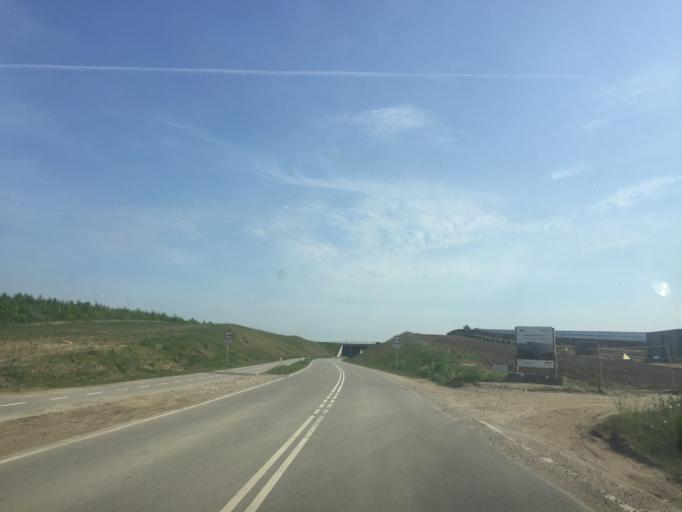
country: DK
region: Capital Region
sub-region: Egedal Kommune
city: Smorumnedre
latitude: 55.7212
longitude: 12.2934
